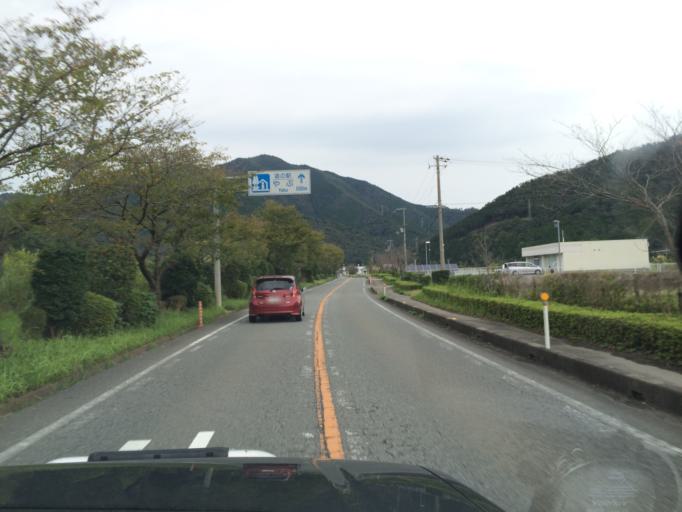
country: JP
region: Hyogo
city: Toyooka
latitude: 35.3776
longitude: 134.8136
